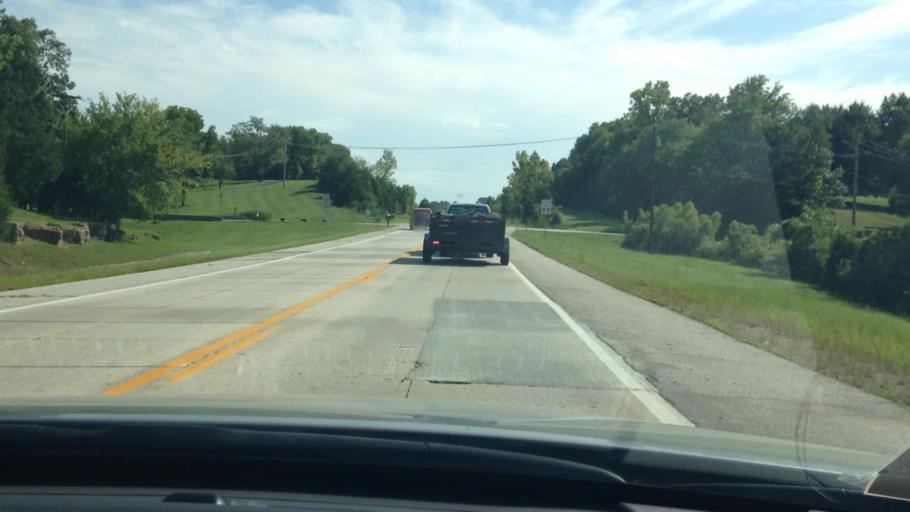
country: US
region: Missouri
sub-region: Jackson County
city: Grandview
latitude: 38.8593
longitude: -94.5858
